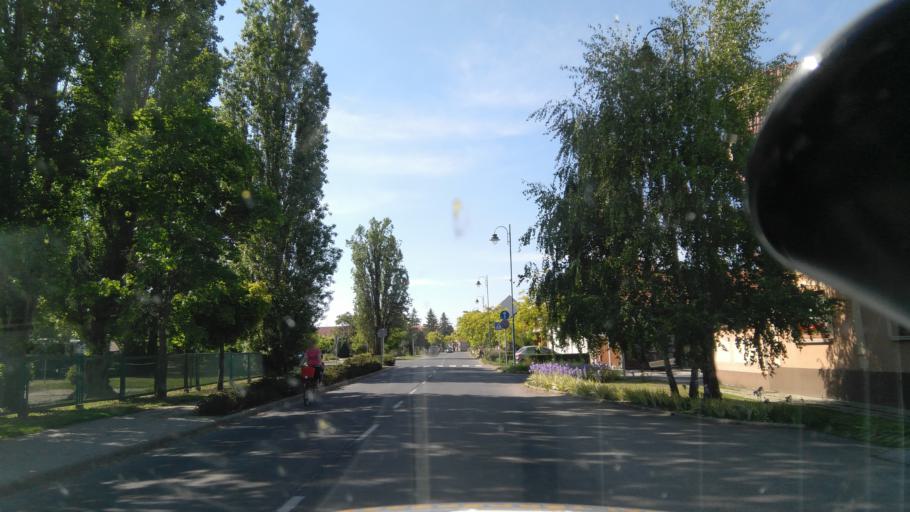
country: HU
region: Bekes
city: Gyula
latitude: 46.6457
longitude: 21.2901
